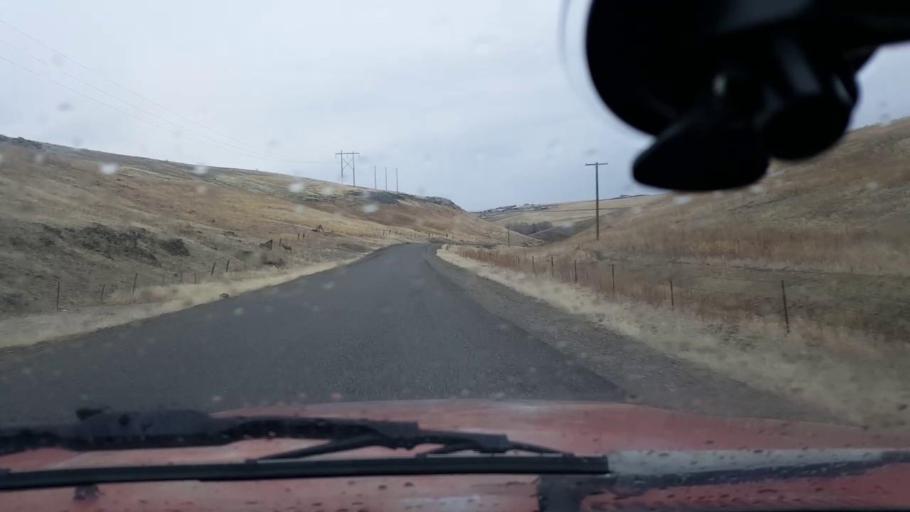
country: US
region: Washington
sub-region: Asotin County
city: Clarkston Heights-Vineland
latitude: 46.3901
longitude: -117.1412
